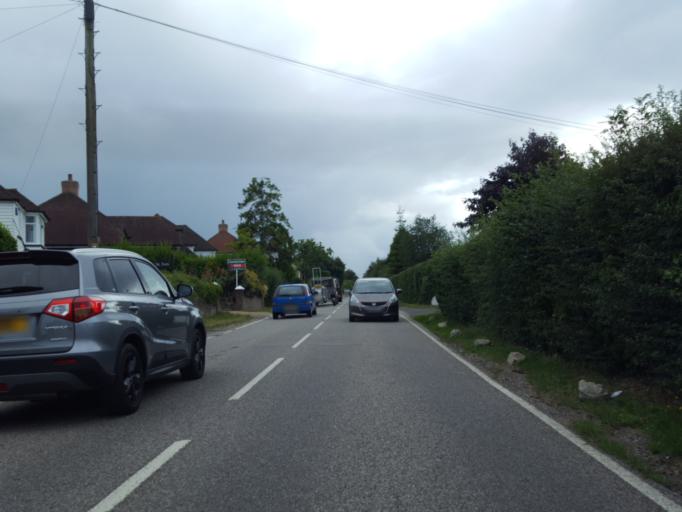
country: GB
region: England
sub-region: Kent
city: Maidstone
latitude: 51.2395
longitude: 0.4875
